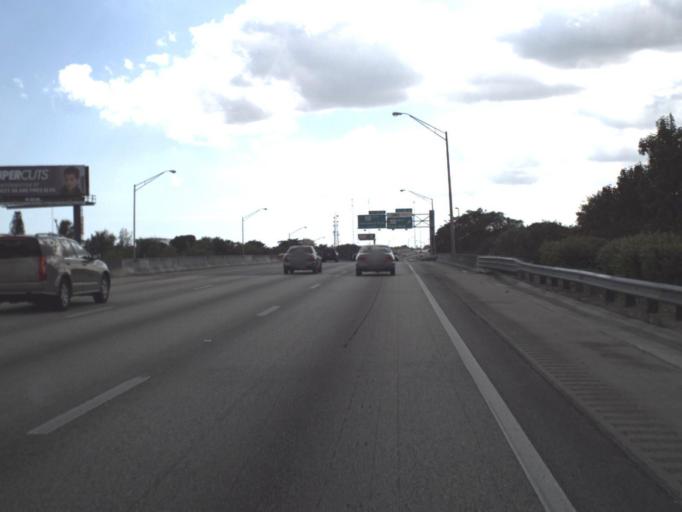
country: US
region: Florida
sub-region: Broward County
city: Pembroke Pines
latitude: 26.0183
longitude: -80.2130
